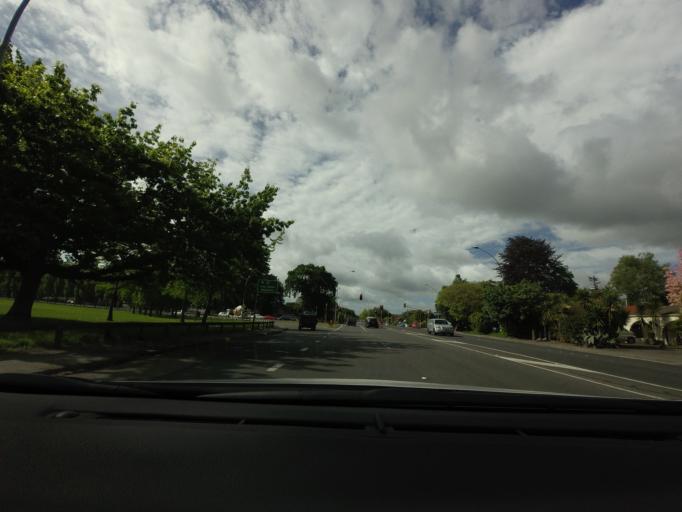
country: NZ
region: Bay of Plenty
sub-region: Rotorua District
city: Rotorua
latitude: -38.1362
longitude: 176.2351
